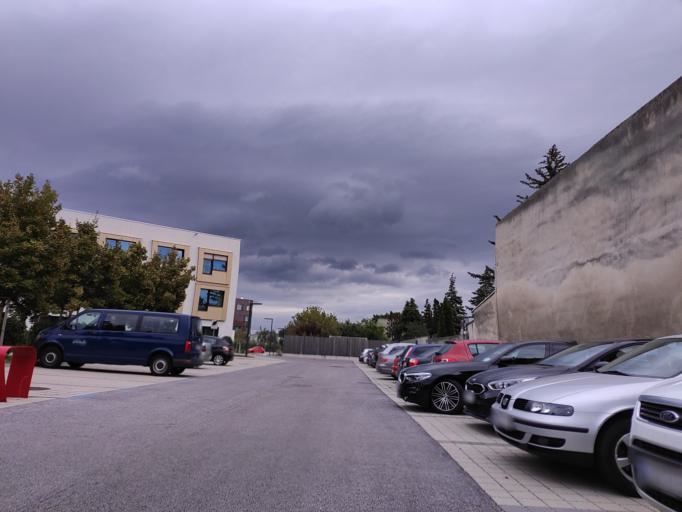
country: AT
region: Lower Austria
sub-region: Politischer Bezirk Baden
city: Baden
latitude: 48.0001
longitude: 16.2517
